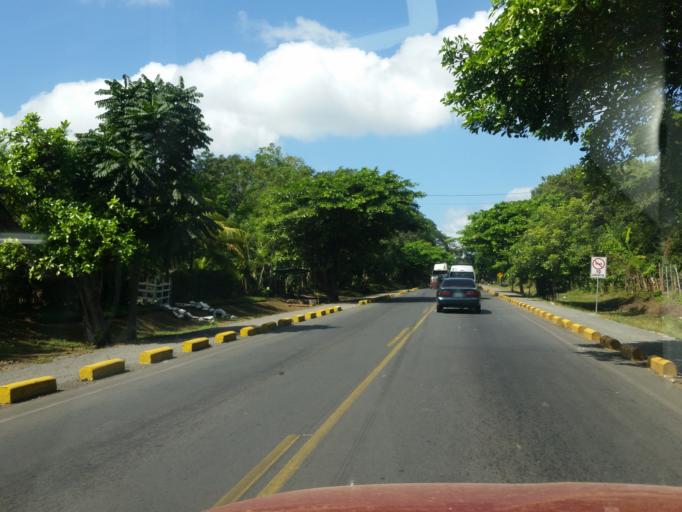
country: NI
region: Granada
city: Diriomo
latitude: 11.8546
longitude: -86.0246
